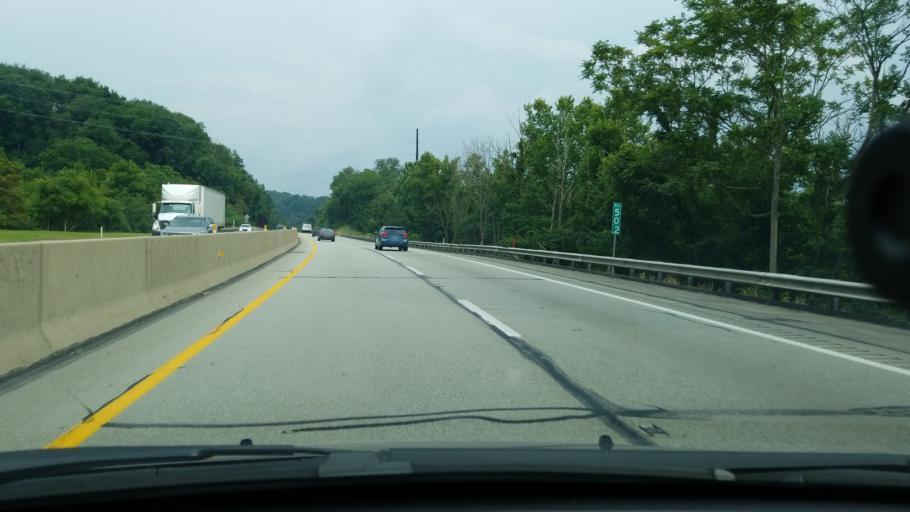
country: US
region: Pennsylvania
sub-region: Allegheny County
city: Cheswick
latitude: 40.5164
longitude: -79.8000
